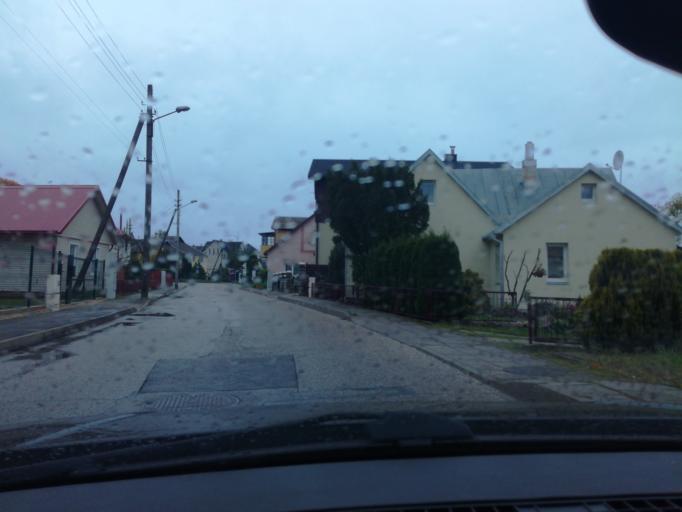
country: LT
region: Alytaus apskritis
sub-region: Alytus
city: Alytus
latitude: 54.3994
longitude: 24.0533
